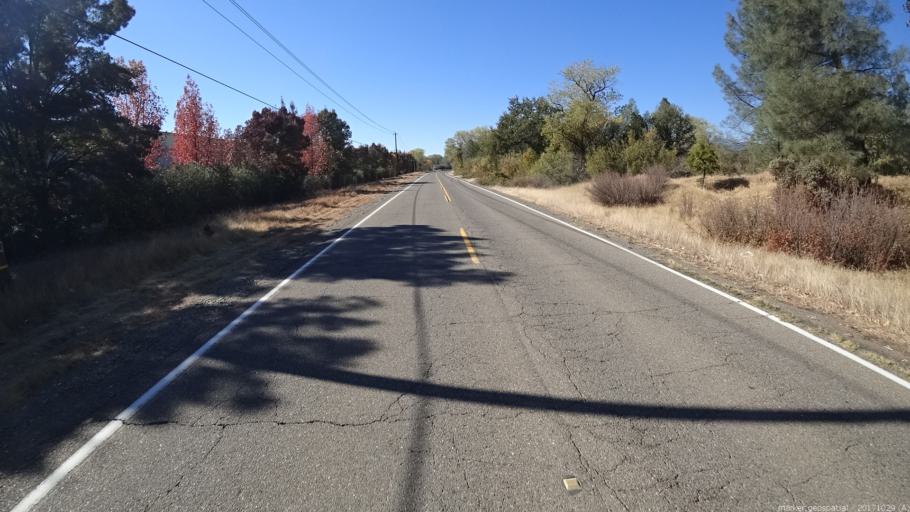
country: US
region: California
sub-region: Shasta County
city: Redding
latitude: 40.5010
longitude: -122.4394
